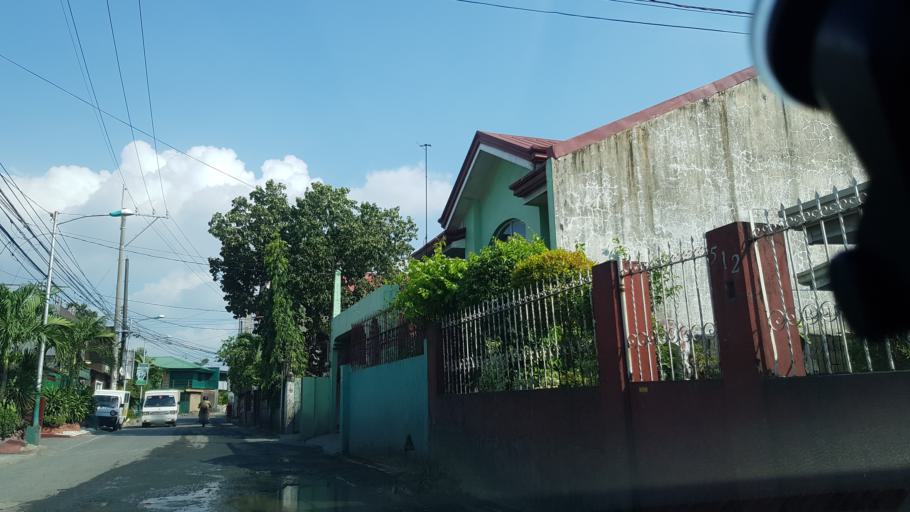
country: PH
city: Sambayanihan People's Village
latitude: 14.4993
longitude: 121.0116
